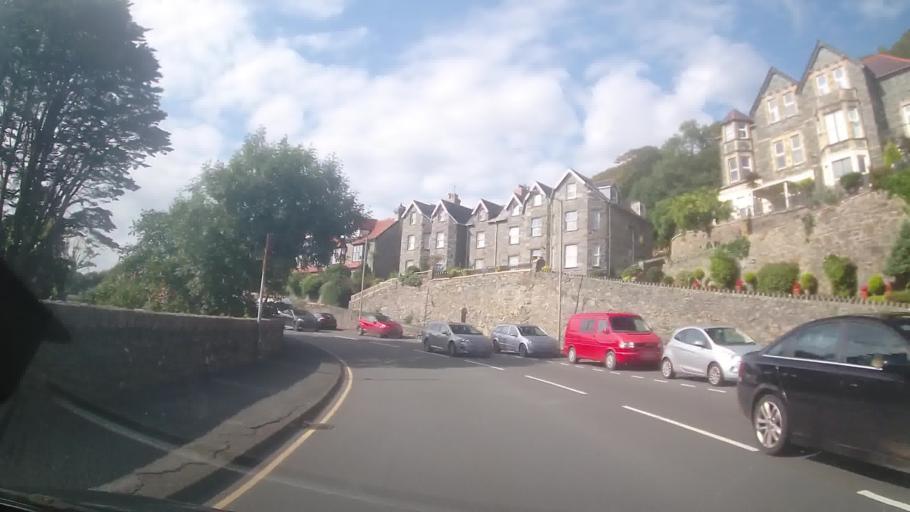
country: GB
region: Wales
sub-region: Gwynedd
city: Barmouth
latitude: 52.7272
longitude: -4.0579
